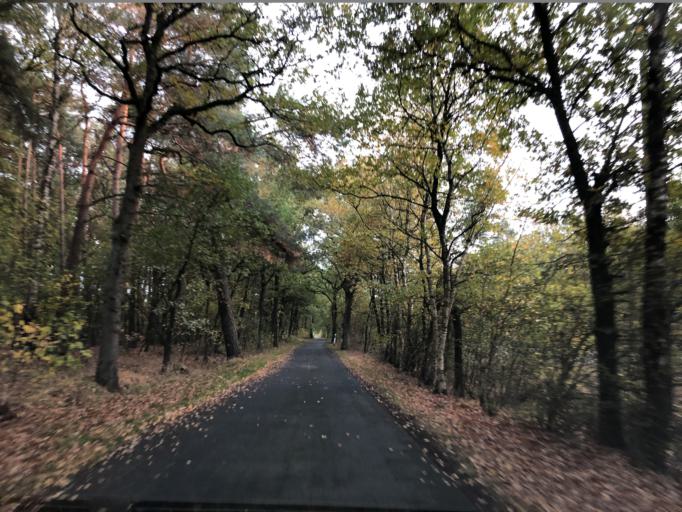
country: DE
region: Lower Saxony
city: Lehe
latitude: 53.0235
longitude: 7.3417
